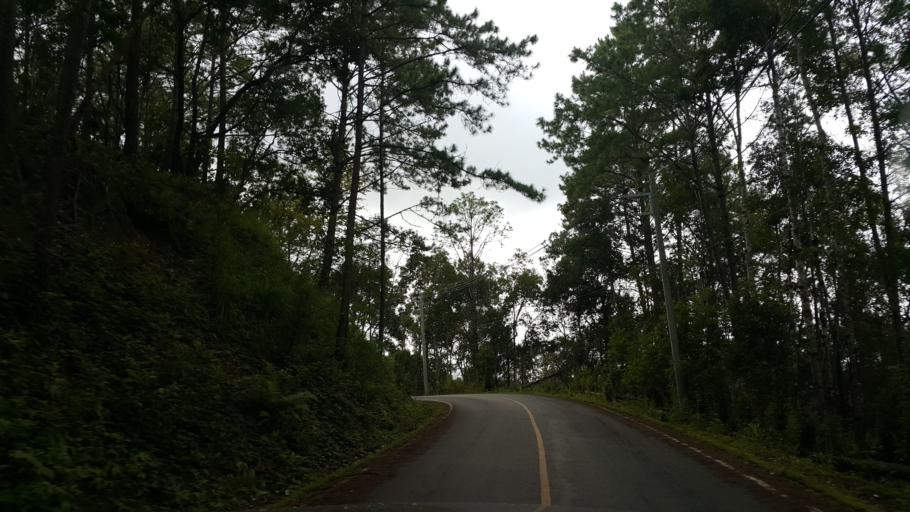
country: TH
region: Chiang Mai
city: Samoeng
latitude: 18.9131
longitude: 98.4995
